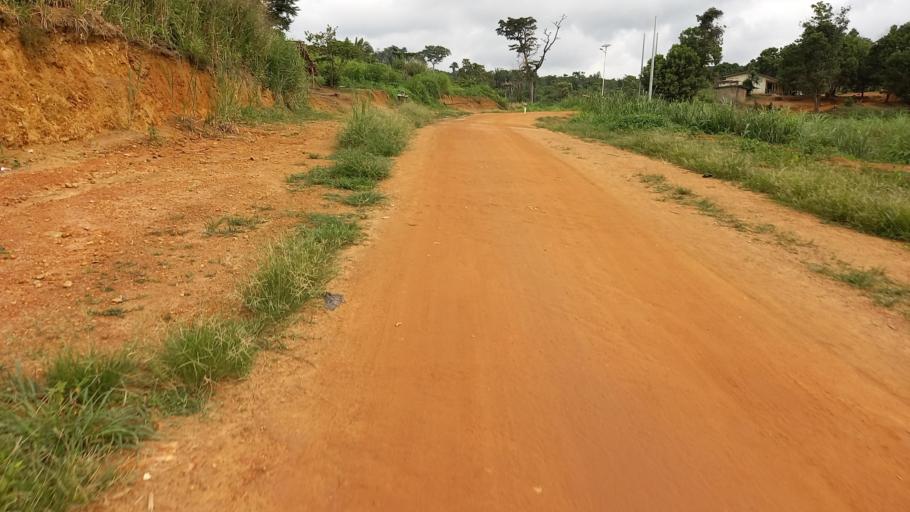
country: SL
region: Eastern Province
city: Kailahun
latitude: 8.2933
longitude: -10.5758
